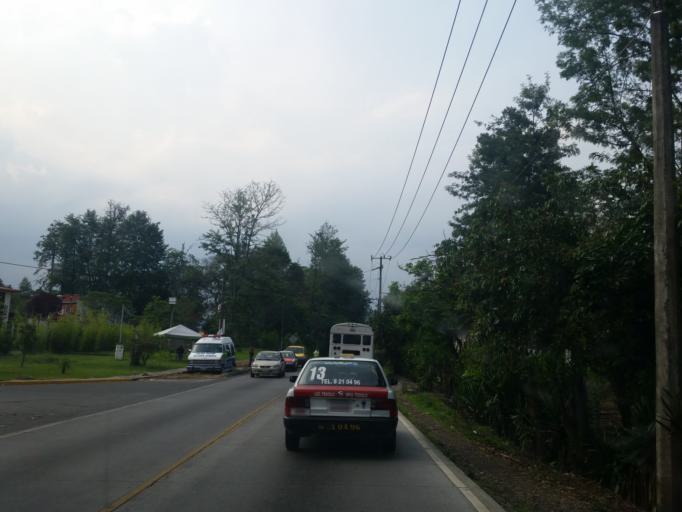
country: MX
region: Veracruz
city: Coatepec
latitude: 19.4437
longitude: -96.9538
